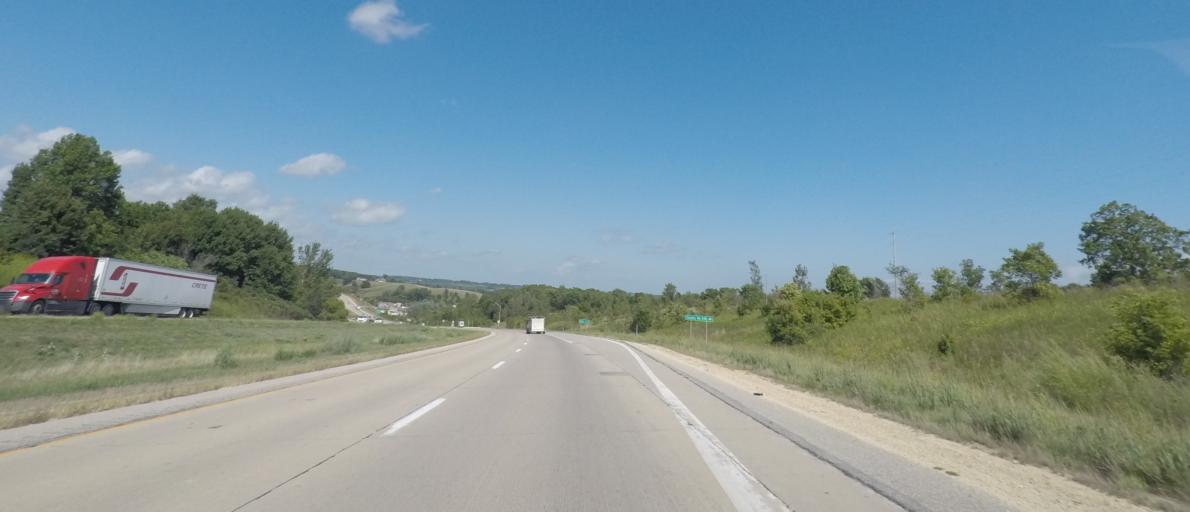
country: US
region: Iowa
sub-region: Jones County
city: Anamosa
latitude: 42.0789
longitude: -91.2757
